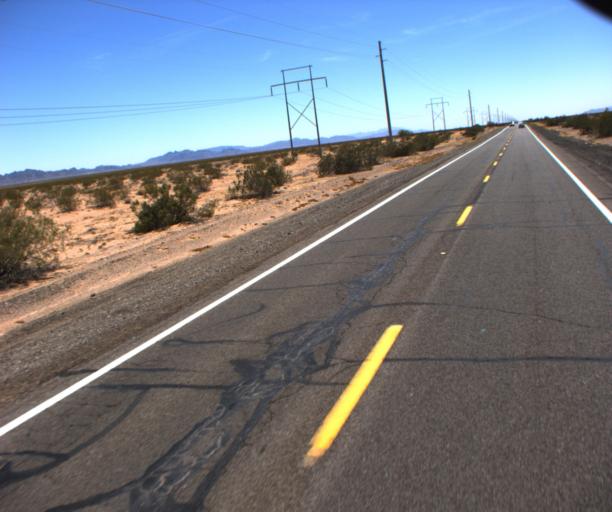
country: US
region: Arizona
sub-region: La Paz County
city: Parker
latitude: 33.9163
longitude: -114.2169
